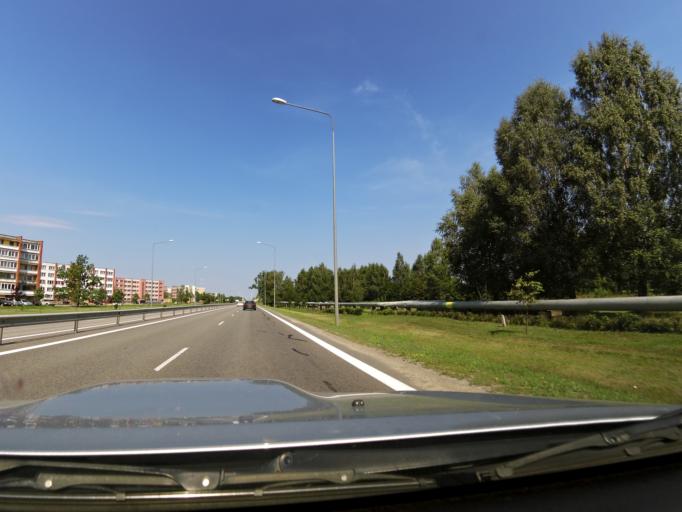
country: LT
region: Siauliu apskritis
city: Radviliskis
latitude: 55.8186
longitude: 23.5371
